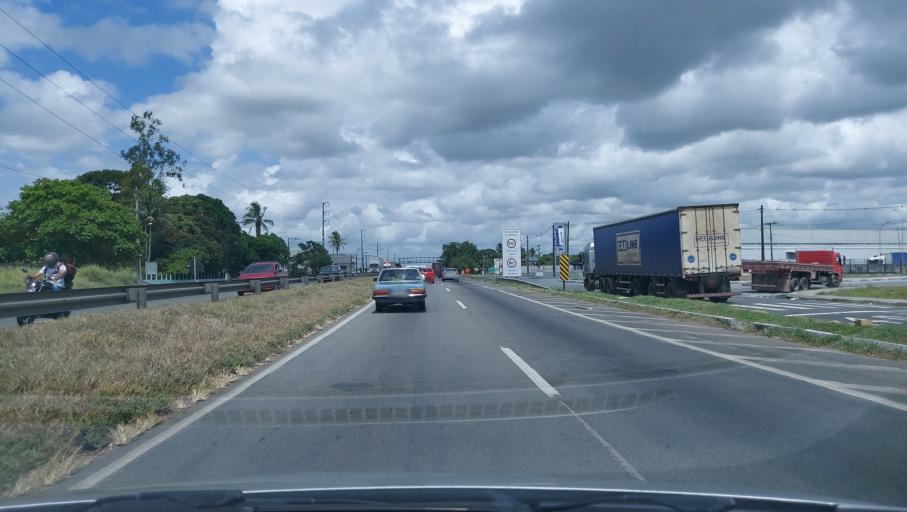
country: BR
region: Bahia
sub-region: Conceicao Do Jacuipe
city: Conceicao do Jacuipe
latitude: -12.3337
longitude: -38.8544
